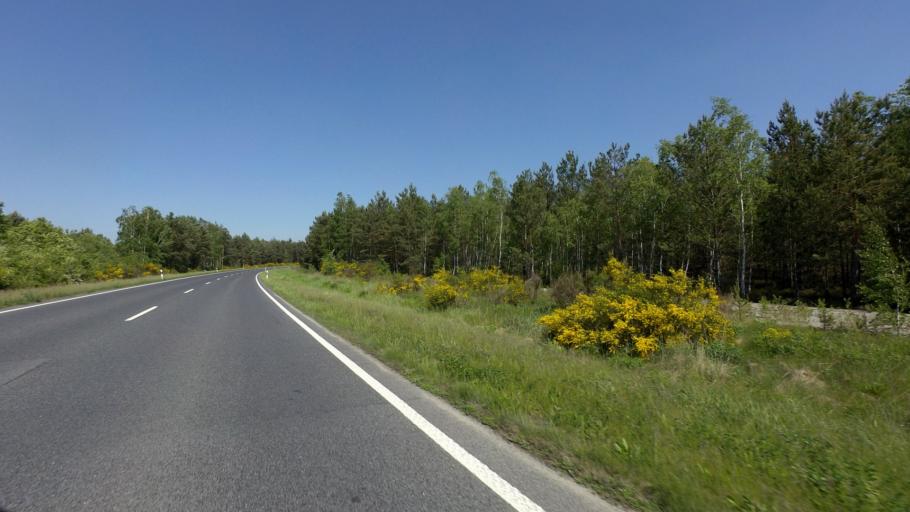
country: DE
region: Brandenburg
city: Spremberg
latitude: 51.5114
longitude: 14.3196
